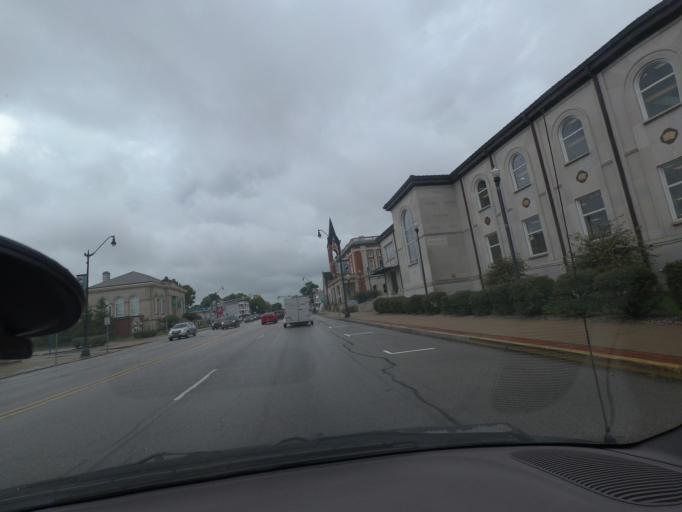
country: US
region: Indiana
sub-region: Montgomery County
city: Crawfordsville
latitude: 40.0404
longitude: -86.9014
